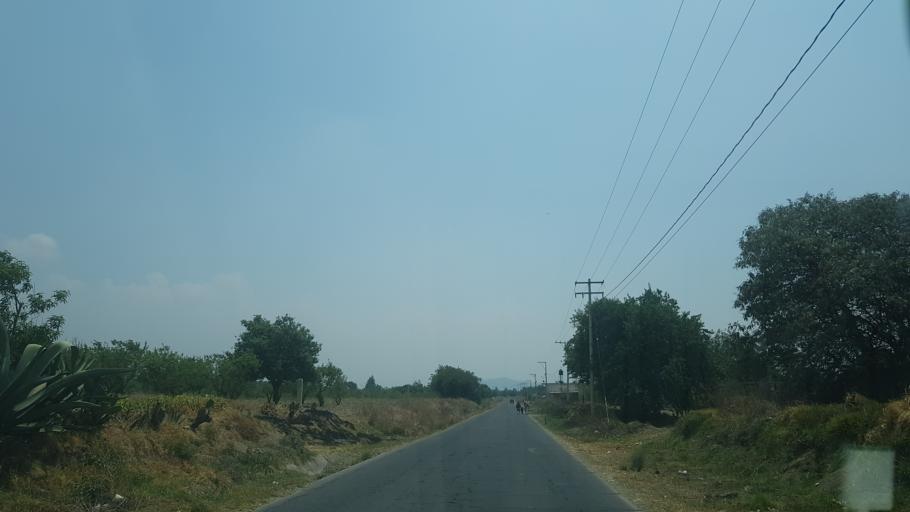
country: MX
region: Puebla
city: San Andres Calpan
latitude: 19.1013
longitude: -98.4415
